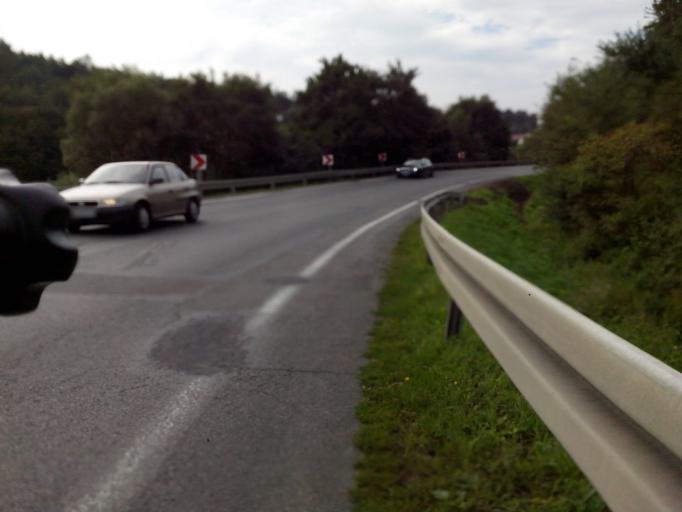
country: PL
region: Subcarpathian Voivodeship
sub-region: Powiat brzozowski
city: Domaradz
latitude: 49.7833
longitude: 21.9494
